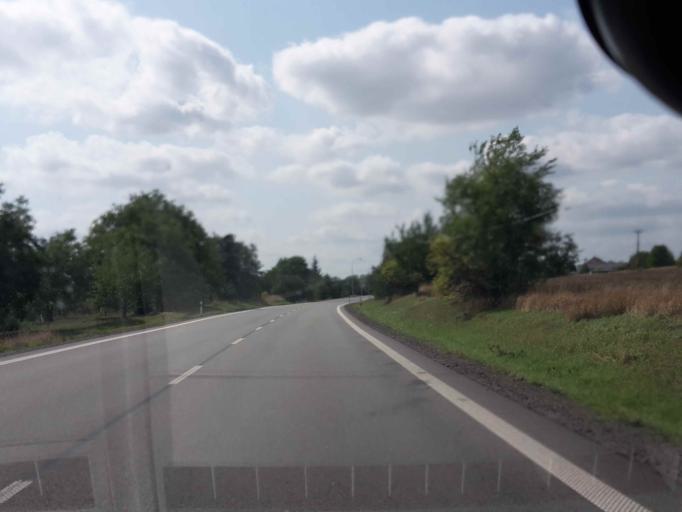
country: CZ
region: South Moravian
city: Rousinov
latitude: 49.2100
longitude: 16.8965
